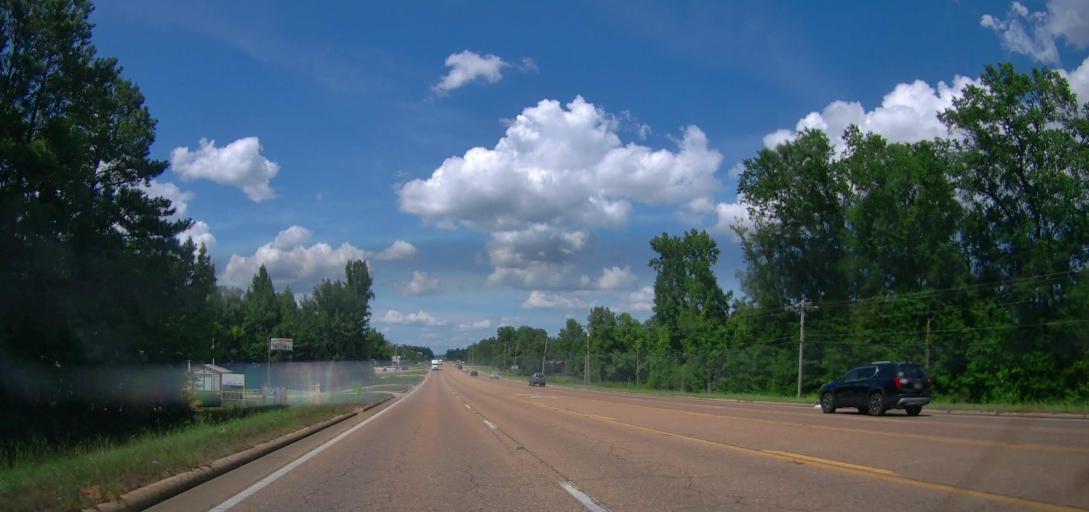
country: US
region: Mississippi
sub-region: Lowndes County
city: Columbus
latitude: 33.5689
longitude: -88.4319
